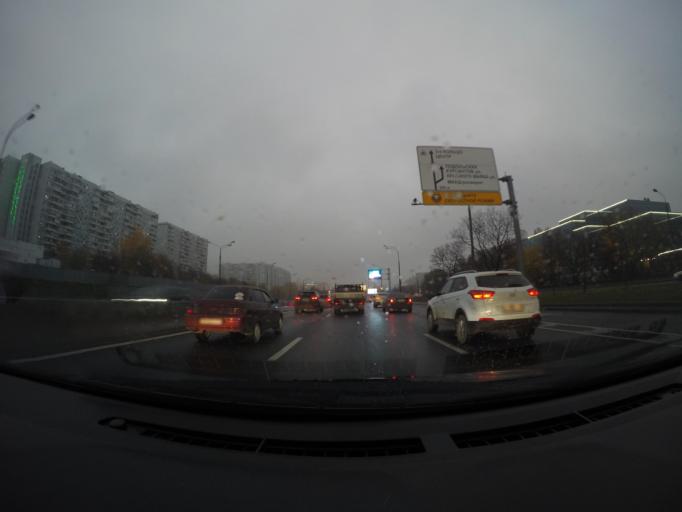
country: RU
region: Moscow
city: Chertanovo Yuzhnoye
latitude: 55.6031
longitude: 37.6058
